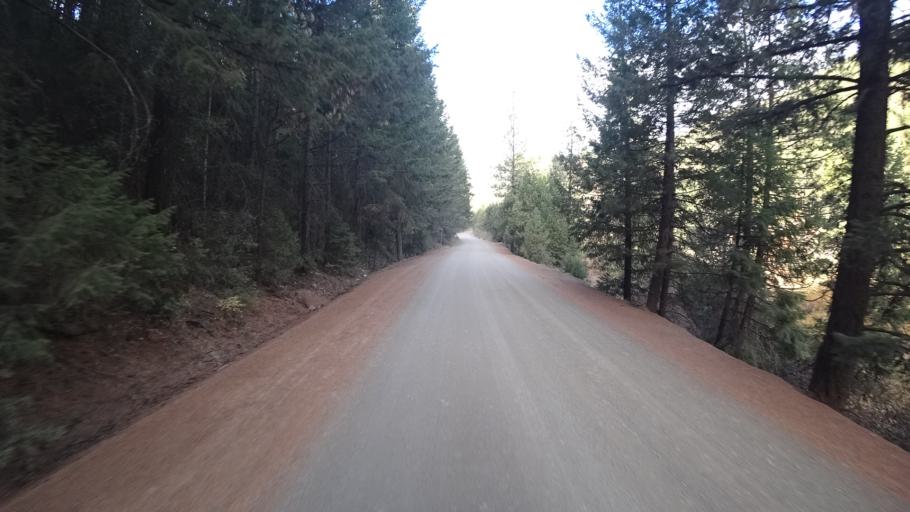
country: US
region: California
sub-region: Siskiyou County
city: Yreka
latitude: 41.7145
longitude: -122.7864
